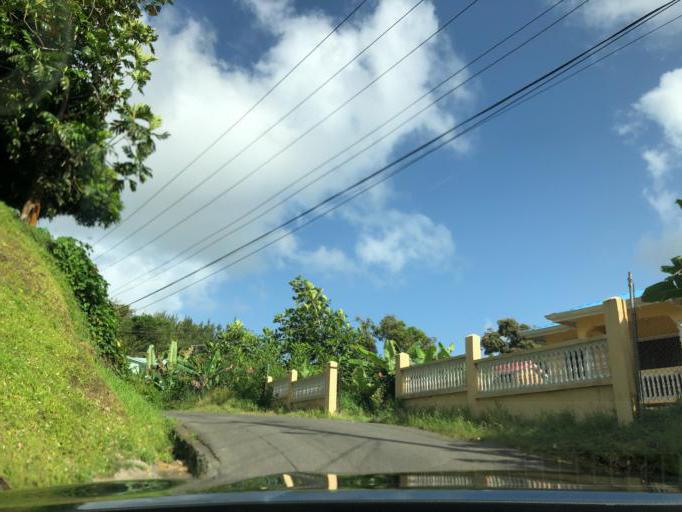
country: LC
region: Castries Quarter
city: Bisee
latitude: 13.9926
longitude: -60.9667
